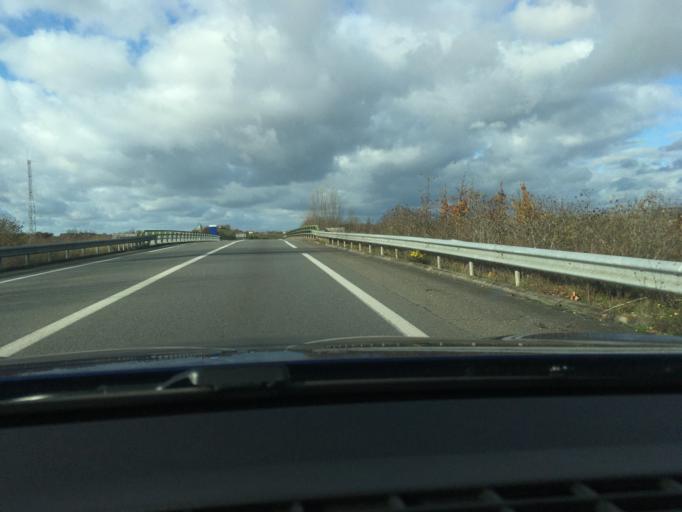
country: FR
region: Midi-Pyrenees
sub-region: Departement du Tarn-et-Garonne
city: Caussade
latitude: 44.1447
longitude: 1.5187
